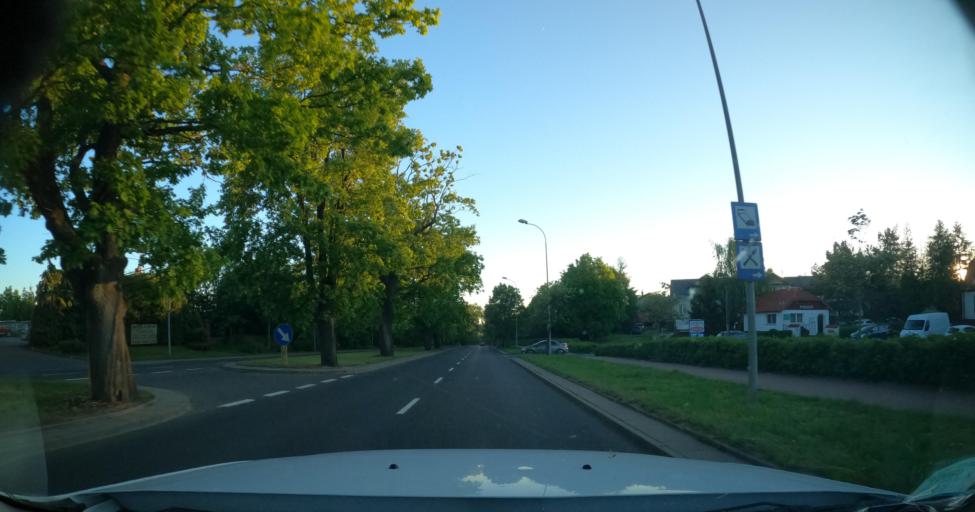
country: PL
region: Pomeranian Voivodeship
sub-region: Slupsk
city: Slupsk
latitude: 54.4670
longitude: 17.0539
